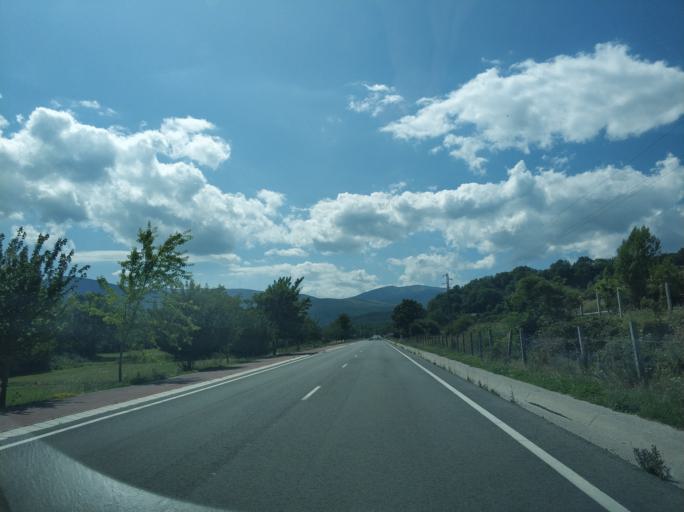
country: ES
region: Cantabria
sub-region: Provincia de Cantabria
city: Villaescusa
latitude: 43.0201
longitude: -4.2468
